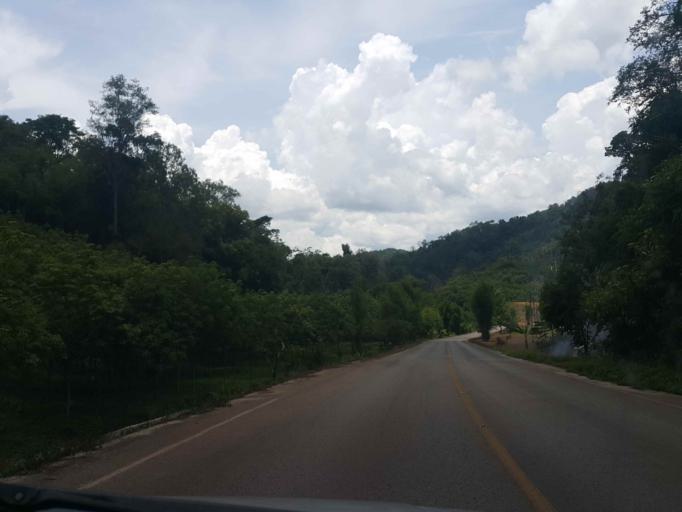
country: TH
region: Phayao
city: Chiang Muan
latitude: 18.9128
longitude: 100.1166
